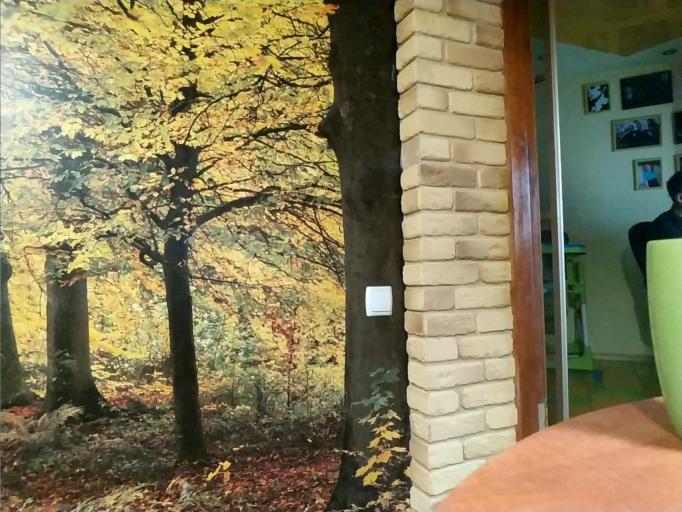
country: RU
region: Tverskaya
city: Staraya Toropa
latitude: 56.3417
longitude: 31.8481
